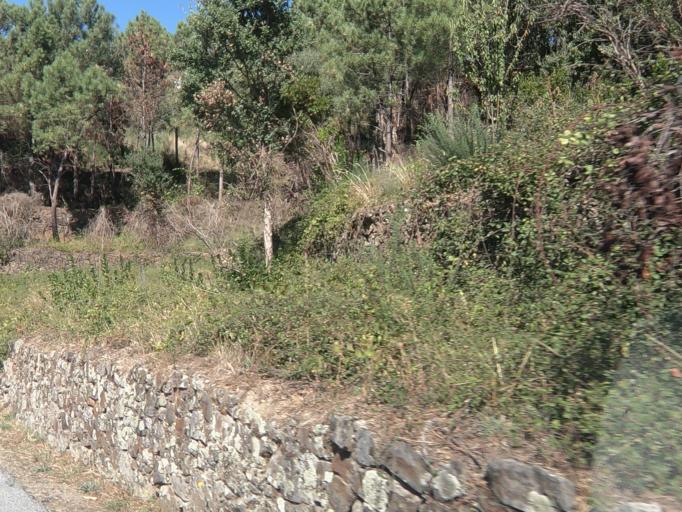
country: PT
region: Vila Real
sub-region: Santa Marta de Penaguiao
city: Santa Marta de Penaguiao
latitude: 41.2572
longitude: -7.7899
